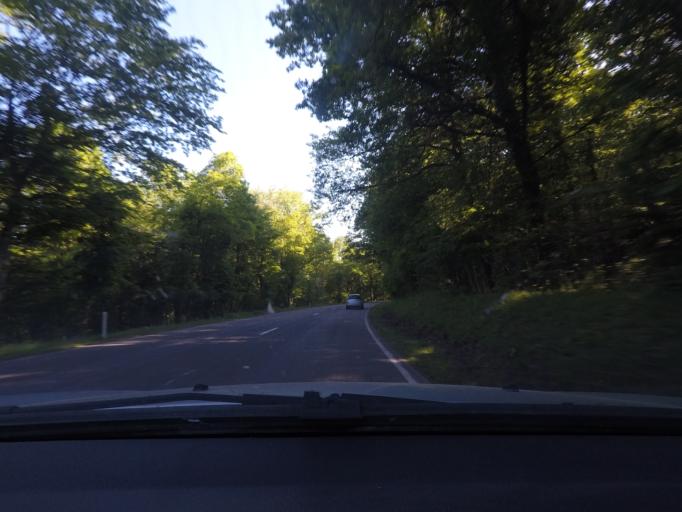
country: BE
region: Wallonia
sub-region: Province de Namur
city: Rochefort
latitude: 50.1933
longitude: 5.1294
